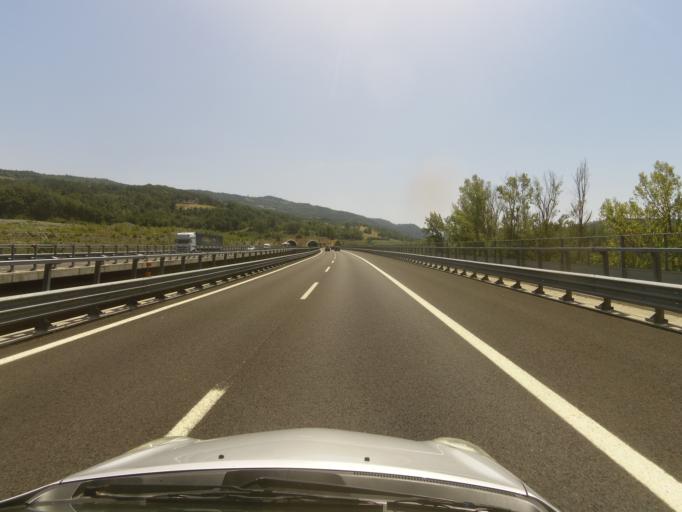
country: IT
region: Emilia-Romagna
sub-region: Provincia di Bologna
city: Grizzana
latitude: 44.2628
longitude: 11.1876
